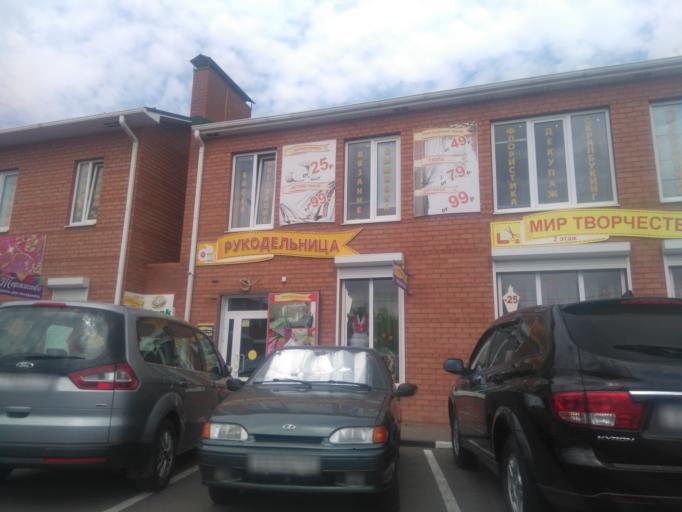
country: RU
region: Krasnodarskiy
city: Tikhoretsk
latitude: 45.8500
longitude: 40.1316
